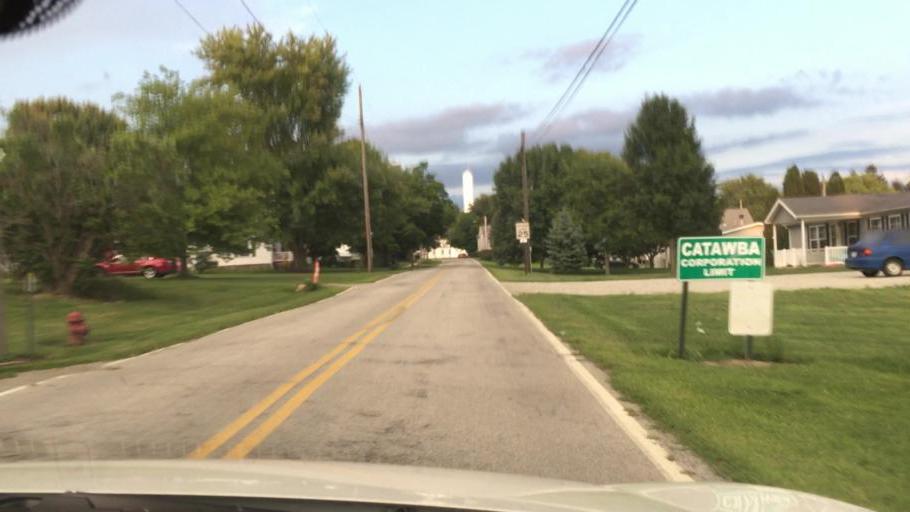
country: US
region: Ohio
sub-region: Champaign County
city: Mechanicsburg
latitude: 39.9985
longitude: -83.6258
